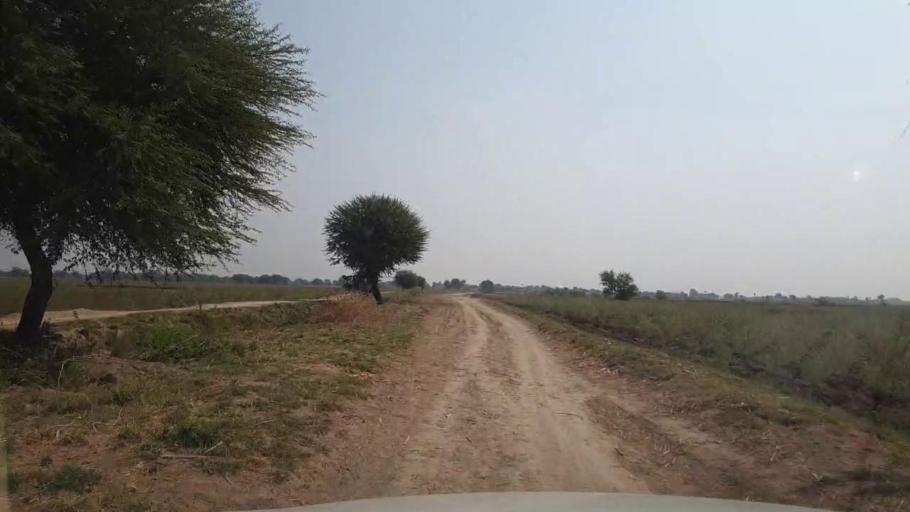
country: PK
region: Sindh
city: Chor
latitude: 25.4524
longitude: 69.6913
